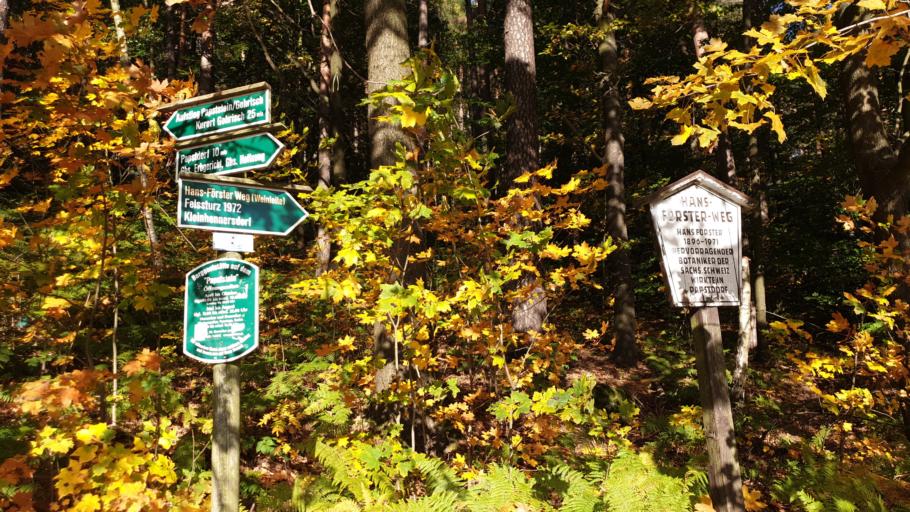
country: DE
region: Saxony
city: Kurort Gohrisch
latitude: 50.8997
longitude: 14.1183
